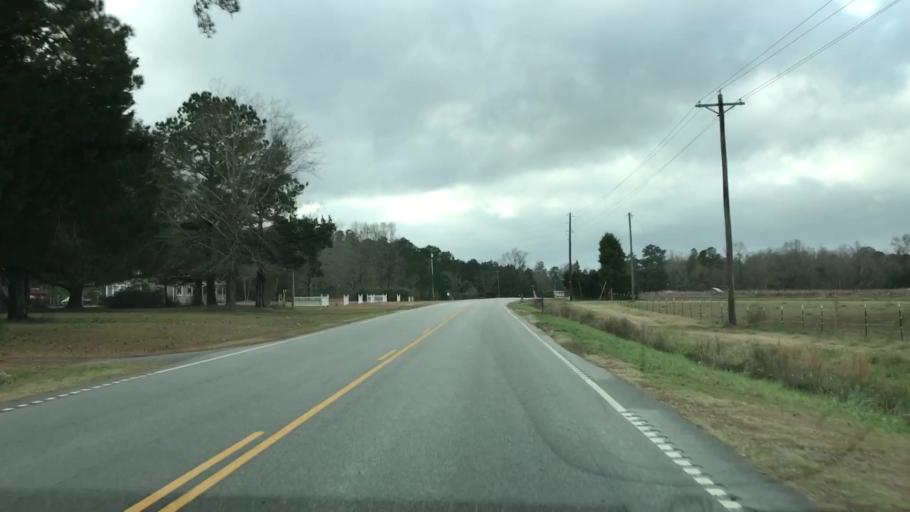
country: US
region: South Carolina
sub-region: Berkeley County
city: Saint Stephen
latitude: 33.2819
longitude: -79.7268
